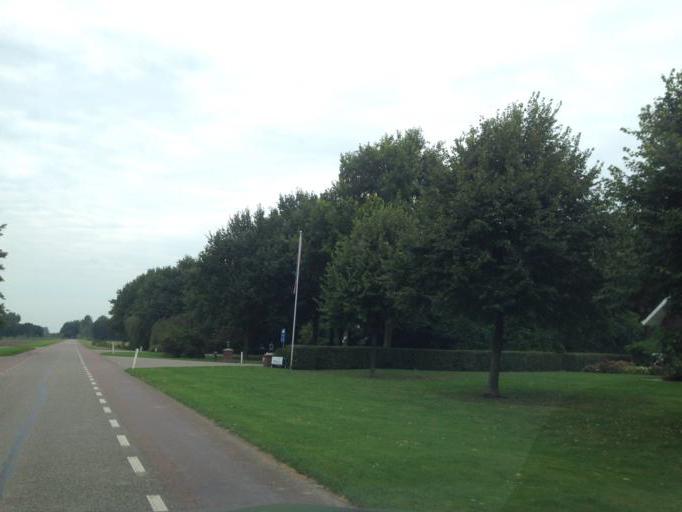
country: NL
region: Flevoland
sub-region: Gemeente Lelystad
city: Lelystad
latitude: 52.4145
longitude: 5.4108
